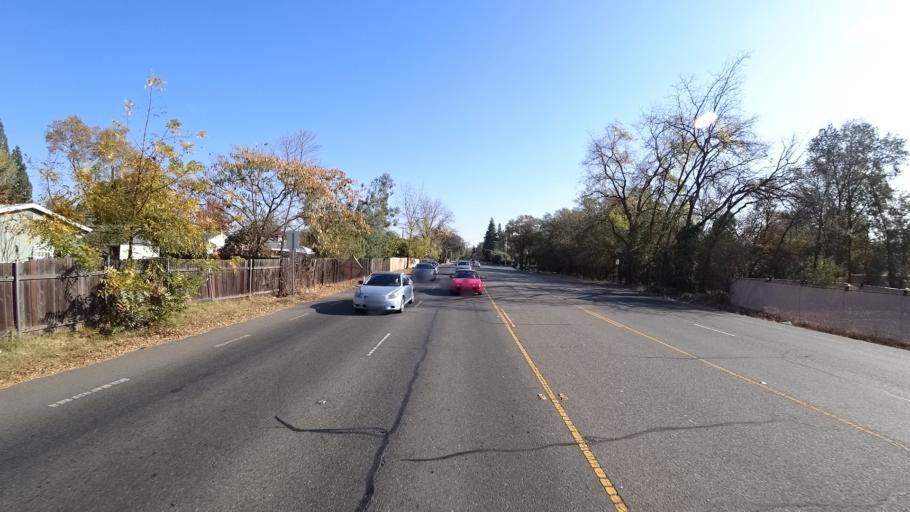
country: US
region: California
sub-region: Sacramento County
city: Citrus Heights
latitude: 38.7056
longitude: -121.2828
